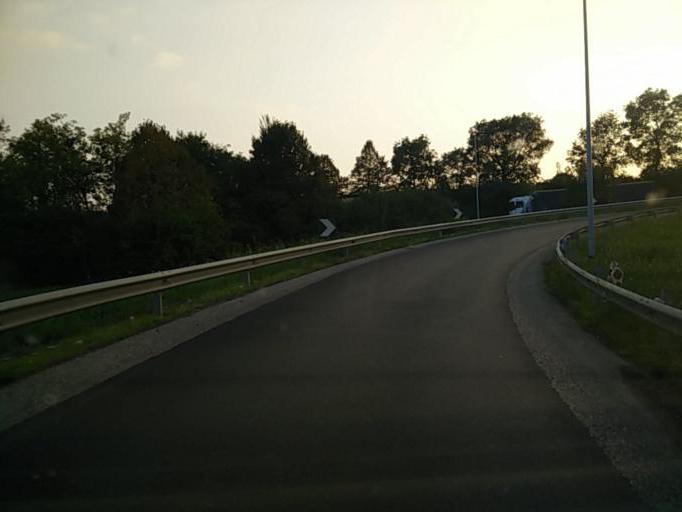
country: IT
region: Veneto
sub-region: Provincia di Verona
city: Caselle
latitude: 45.4294
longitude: 10.9132
